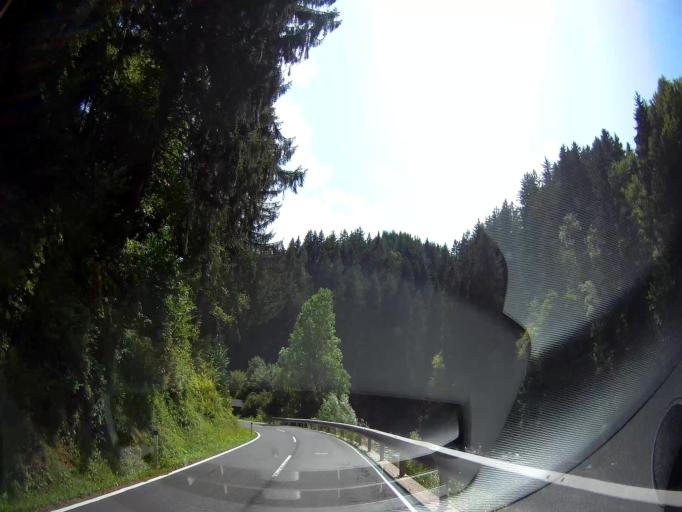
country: AT
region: Carinthia
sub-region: Politischer Bezirk Spittal an der Drau
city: Seeboden
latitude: 46.8514
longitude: 13.5005
